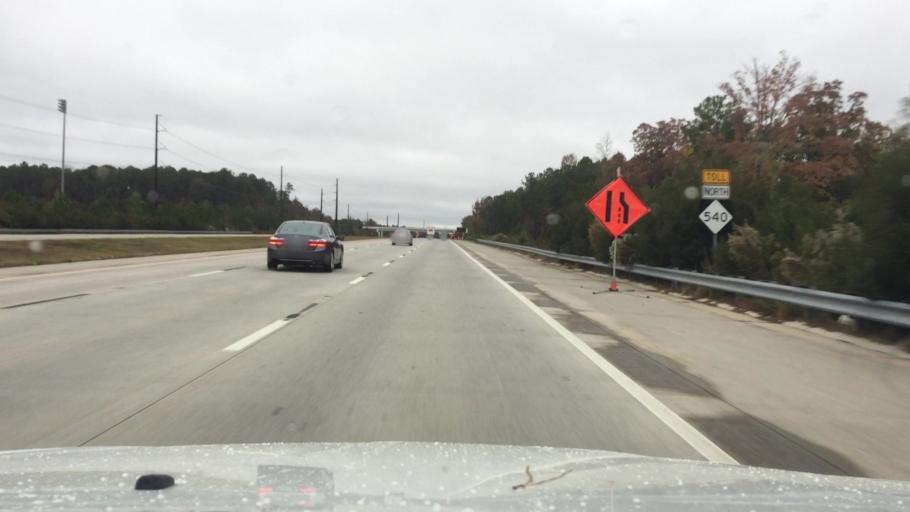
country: US
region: North Carolina
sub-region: Wake County
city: Green Level
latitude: 35.7964
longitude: -78.8895
